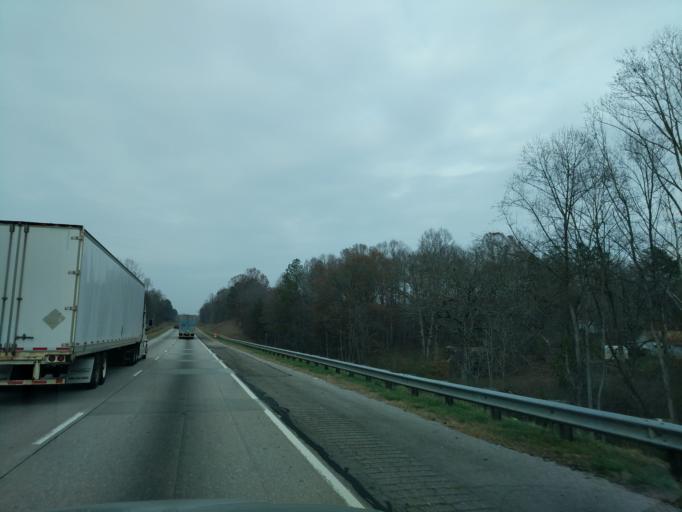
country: US
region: Georgia
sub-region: Jackson County
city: Commerce
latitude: 34.2721
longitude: -83.4376
